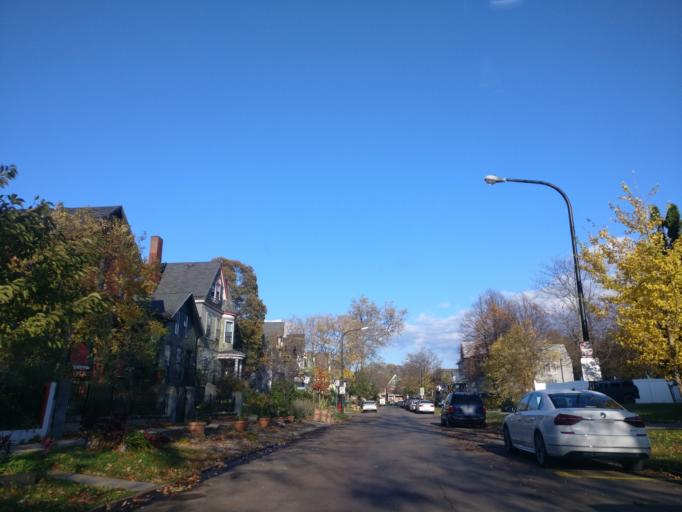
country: US
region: New York
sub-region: Erie County
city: Buffalo
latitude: 42.8991
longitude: -78.8829
